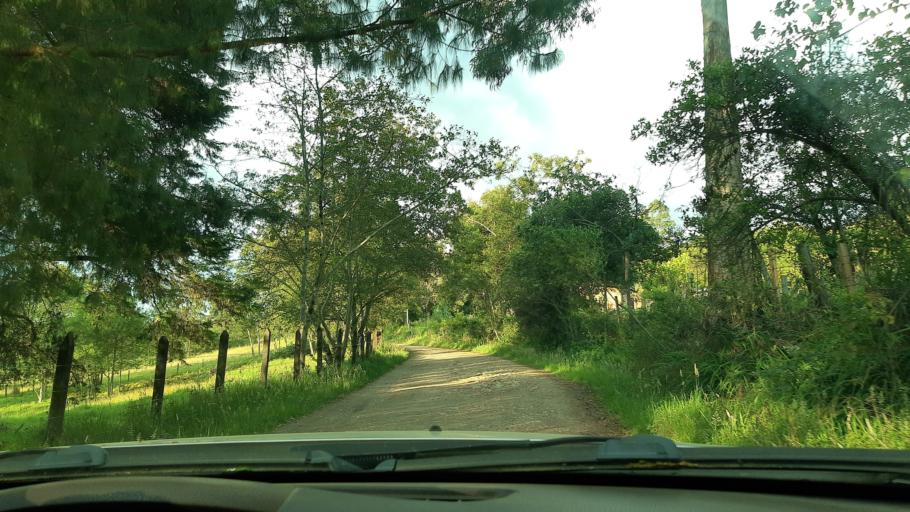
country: CO
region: Boyaca
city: La Capilla
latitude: 5.7008
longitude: -73.4864
